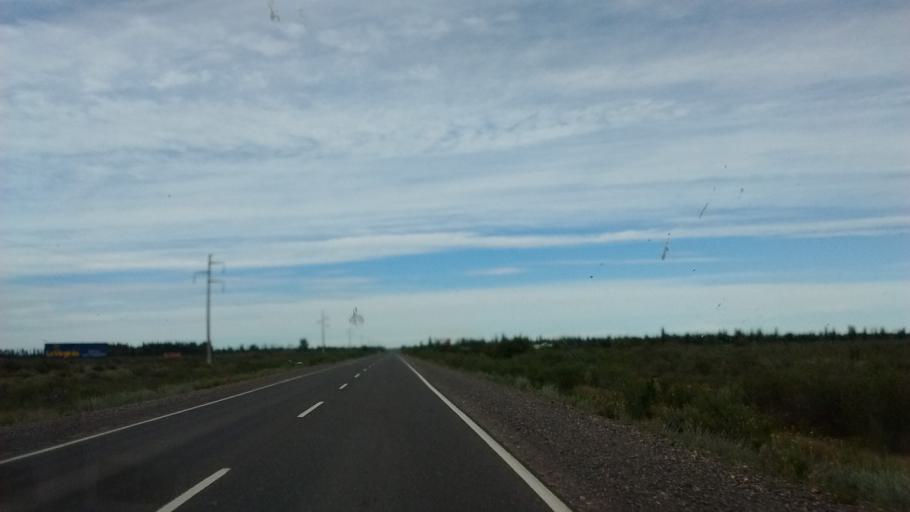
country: AR
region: Rio Negro
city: Contraalmirante Cordero
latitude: -38.6571
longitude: -68.1416
